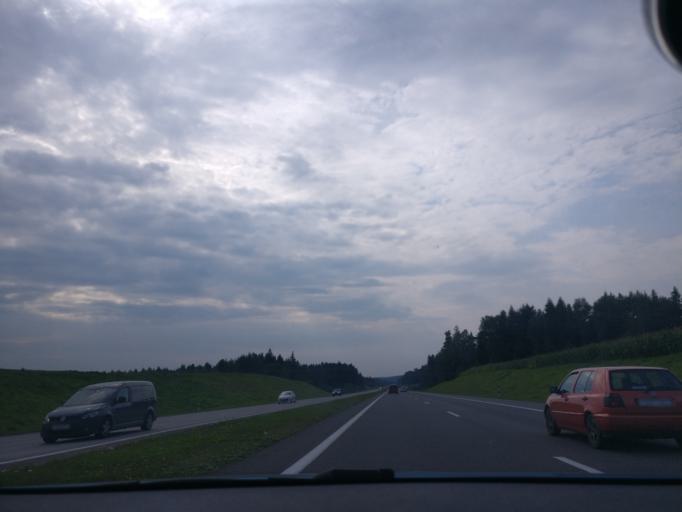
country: BY
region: Minsk
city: Lahoysk
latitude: 54.1416
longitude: 27.8092
